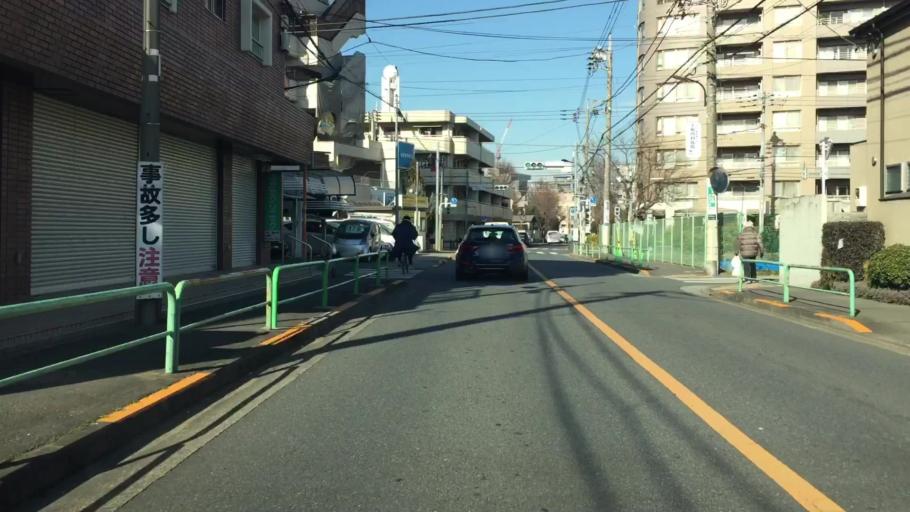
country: JP
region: Saitama
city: Wako
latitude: 35.7579
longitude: 139.6613
